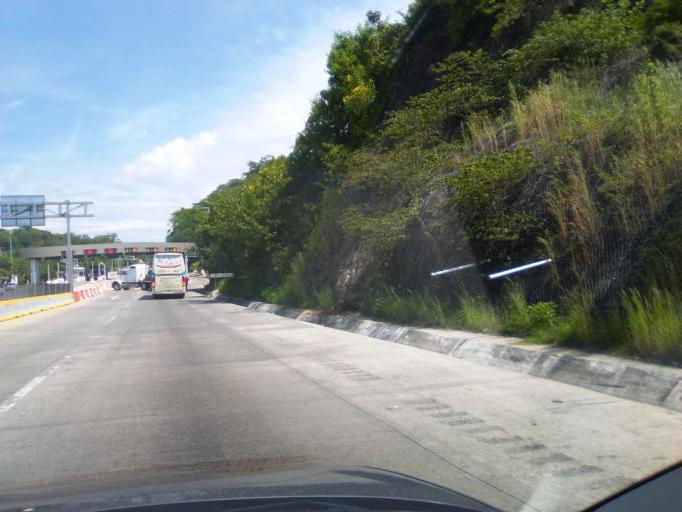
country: MX
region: Guerrero
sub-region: Acapulco de Juarez
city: Colonia Nueva Revolucion
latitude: 16.9276
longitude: -99.8034
